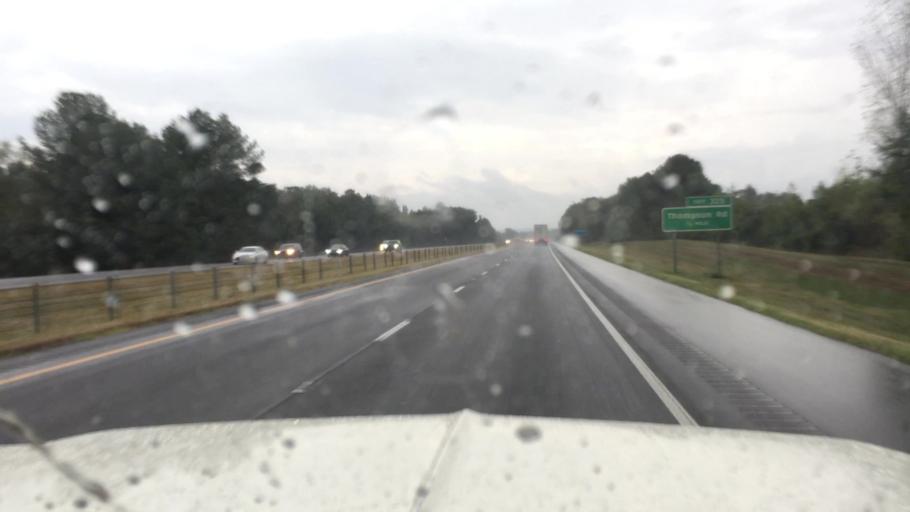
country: US
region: Alabama
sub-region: Morgan County
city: Hartselle
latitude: 34.4239
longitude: -86.8990
